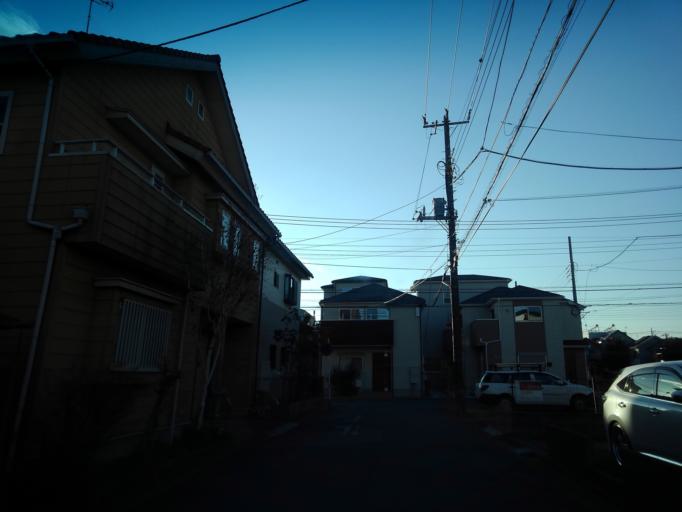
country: JP
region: Saitama
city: Tokorozawa
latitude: 35.8023
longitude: 139.5174
